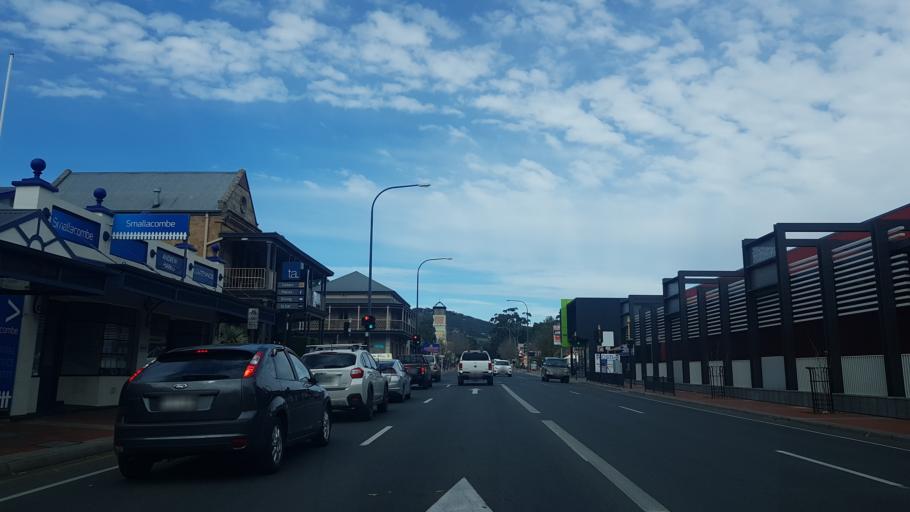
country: AU
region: South Australia
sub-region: Mitcham
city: Hawthorn
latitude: -34.9736
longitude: 138.6092
